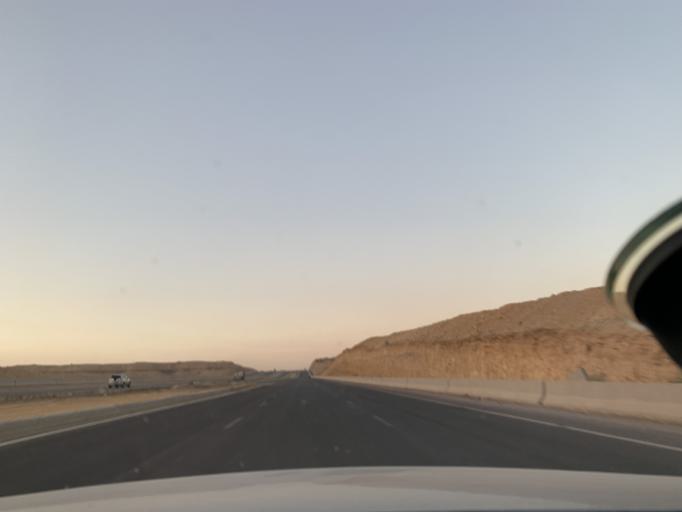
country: EG
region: Muhafazat al Qahirah
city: Halwan
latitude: 29.9429
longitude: 31.5331
